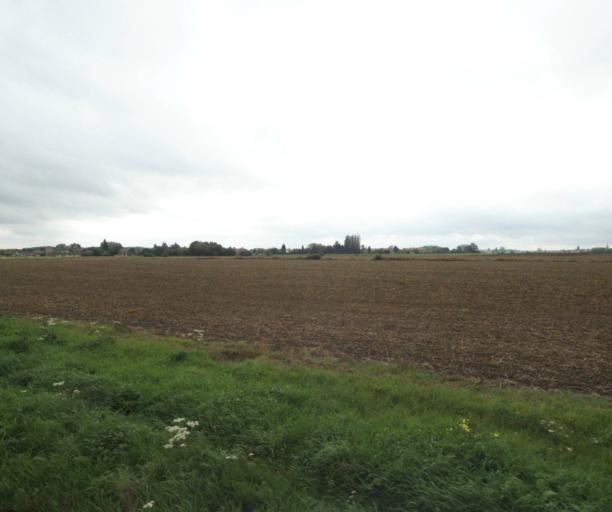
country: FR
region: Nord-Pas-de-Calais
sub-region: Departement du Nord
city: Wavrin
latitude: 50.5708
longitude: 2.9235
